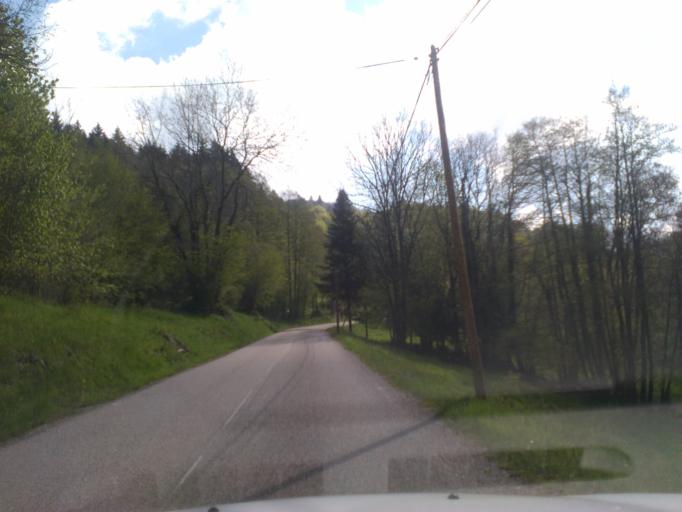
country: FR
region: Lorraine
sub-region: Departement des Vosges
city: Saulxures-sur-Moselotte
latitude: 47.9898
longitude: 6.7698
